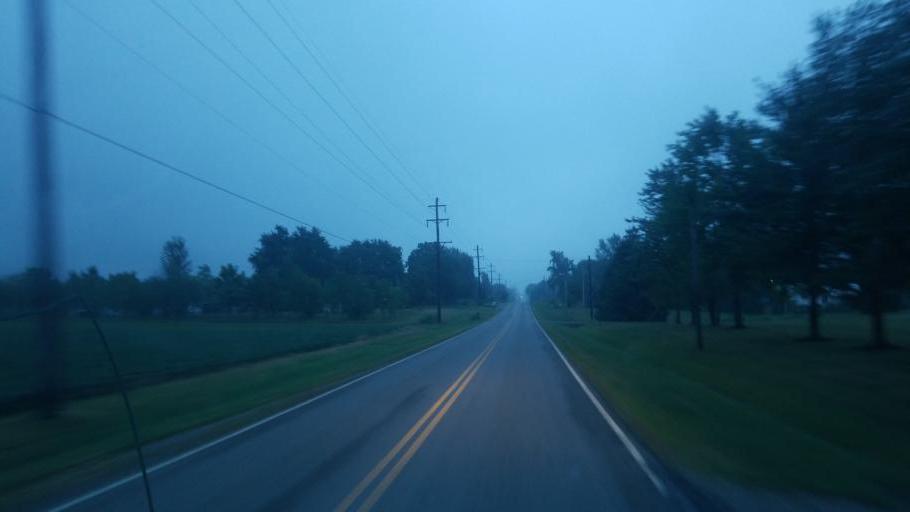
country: US
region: Ohio
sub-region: Defiance County
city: Hicksville
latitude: 41.3236
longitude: -84.7667
